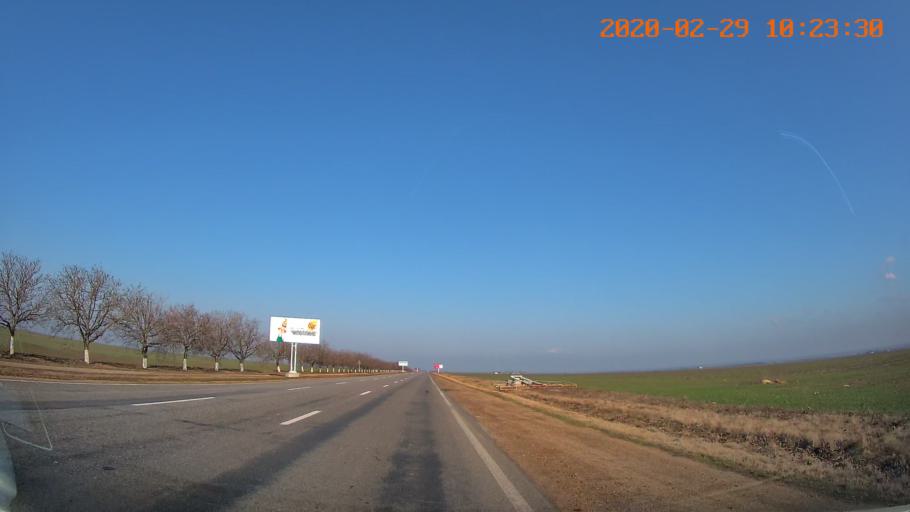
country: MD
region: Telenesti
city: Tiraspolul Nou
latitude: 46.8868
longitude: 29.6019
